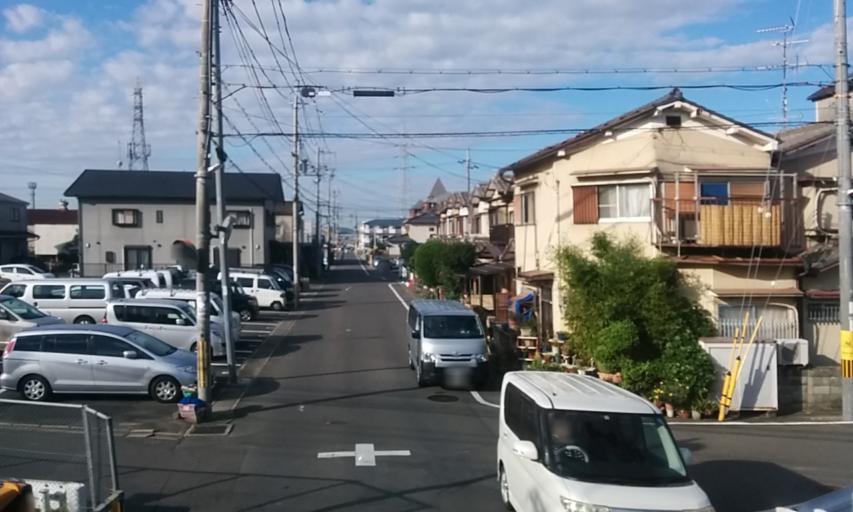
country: JP
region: Kyoto
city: Uji
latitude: 34.9188
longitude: 135.7679
